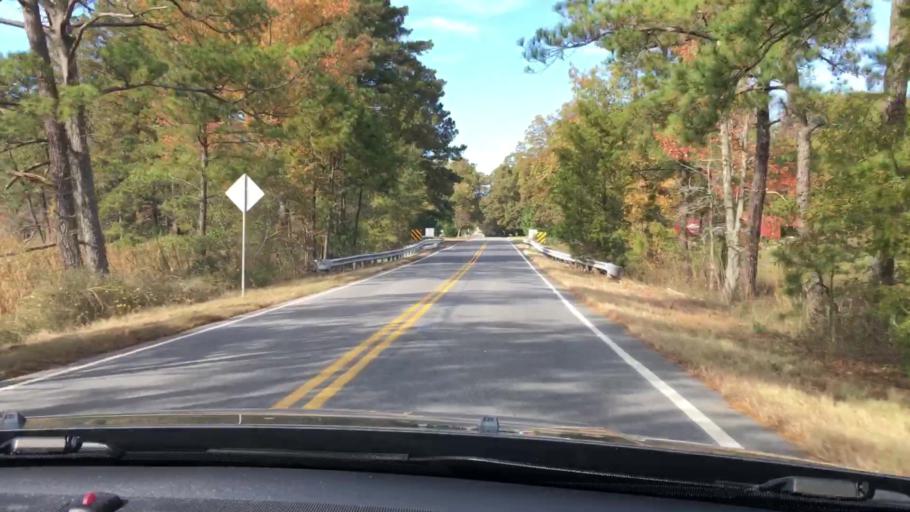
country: US
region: Virginia
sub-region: King William County
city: West Point
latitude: 37.5201
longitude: -76.8232
